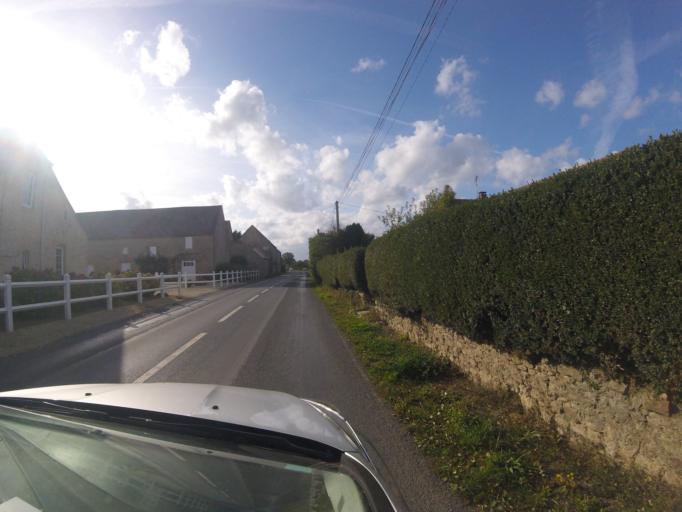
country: FR
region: Lower Normandy
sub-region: Departement du Calvados
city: Port-en-Bessin-Huppain
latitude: 49.3499
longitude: -0.8238
